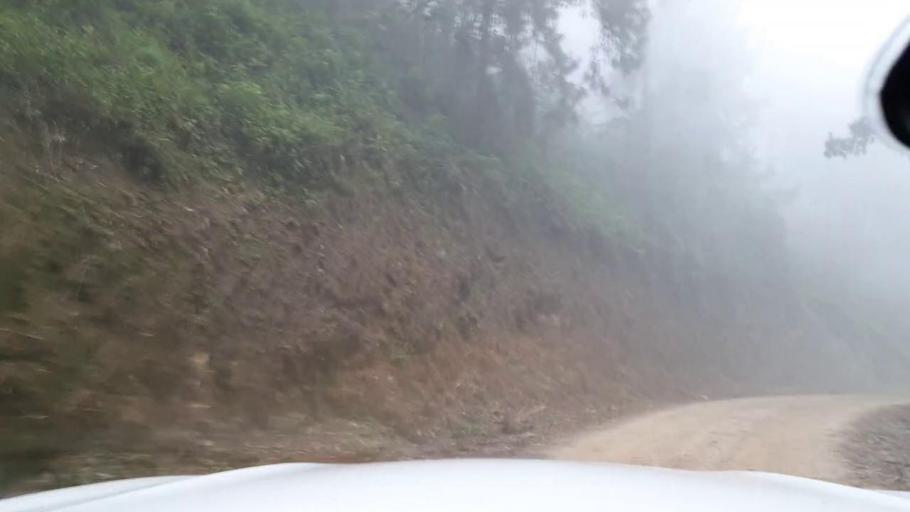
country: BI
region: Cibitoke
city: Cibitoke
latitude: -2.5928
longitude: 29.1942
